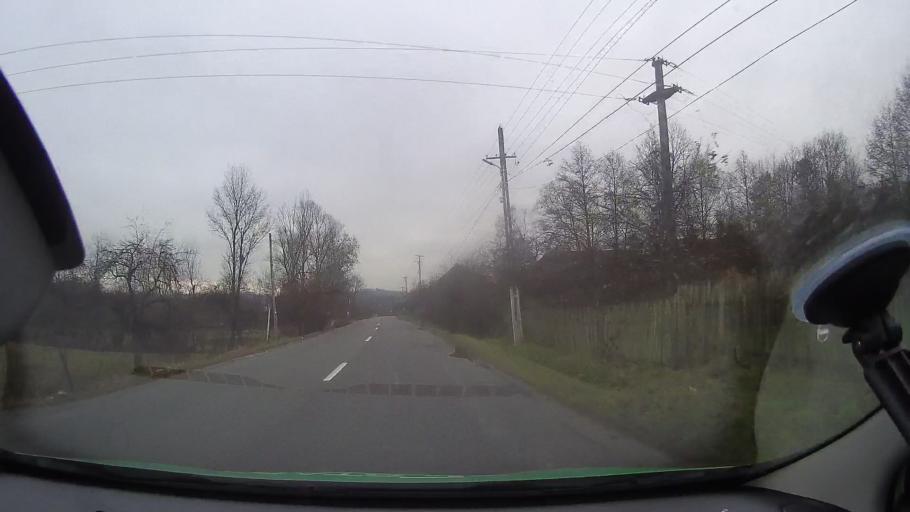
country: RO
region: Arad
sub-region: Comuna Varfurile
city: Varfurile
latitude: 46.3130
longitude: 22.5142
